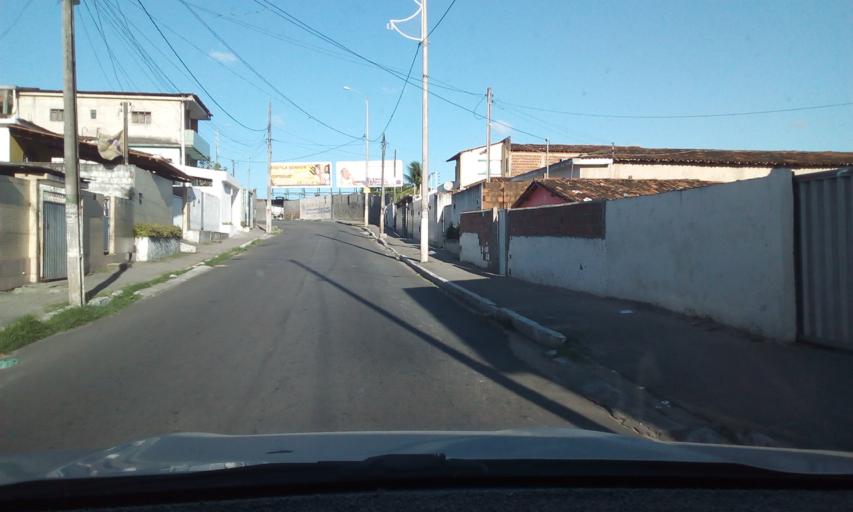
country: BR
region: Paraiba
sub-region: Bayeux
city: Bayeux
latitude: -7.1237
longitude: -34.9112
